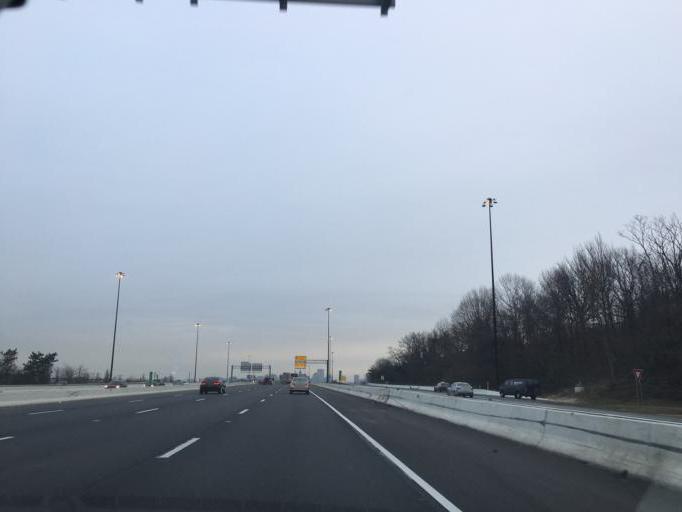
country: US
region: Maryland
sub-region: Baltimore County
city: Lansdowne
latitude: 39.2666
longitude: -76.6649
